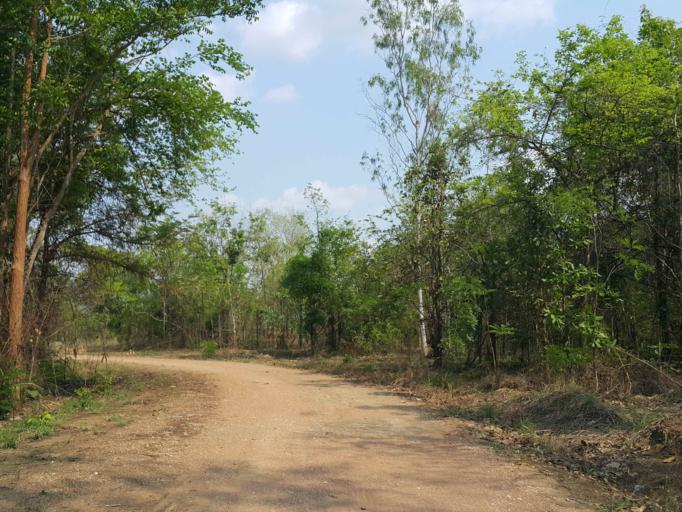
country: TH
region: Sukhothai
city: Thung Saliam
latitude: 17.3359
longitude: 99.4269
